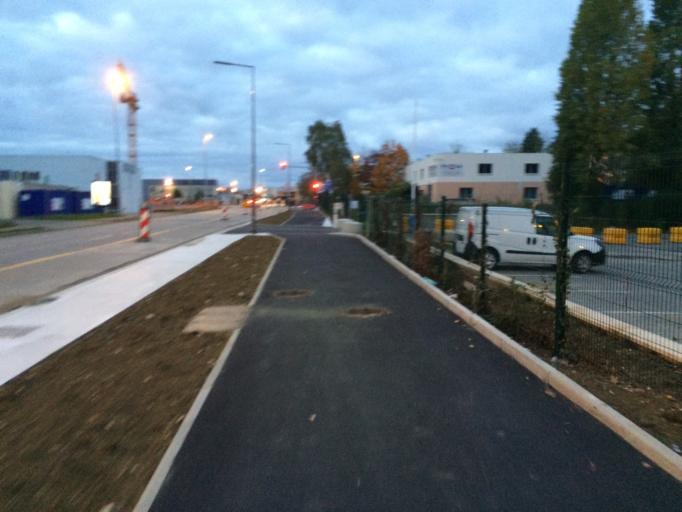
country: FR
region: Ile-de-France
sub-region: Departement de l'Essonne
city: Orsay
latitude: 48.6873
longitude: 2.2061
